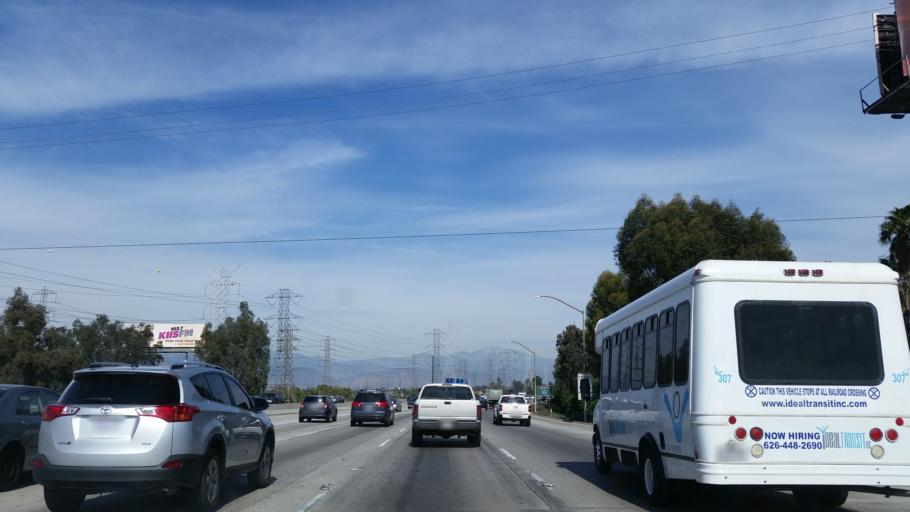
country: US
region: California
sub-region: Los Angeles County
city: South El Monte
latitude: 34.0371
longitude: -118.0229
